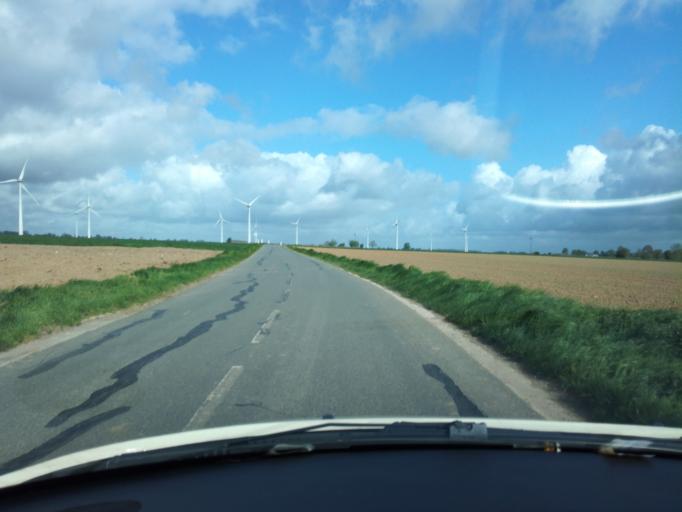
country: FR
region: Picardie
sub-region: Departement de la Somme
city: Beaucamps-le-Vieux
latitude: 49.8779
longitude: 1.8257
